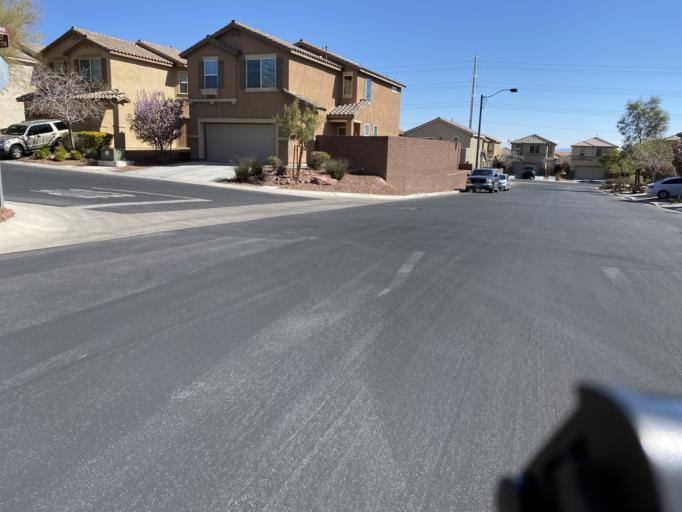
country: US
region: Nevada
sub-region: Clark County
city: Summerlin South
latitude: 36.3020
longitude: -115.3306
